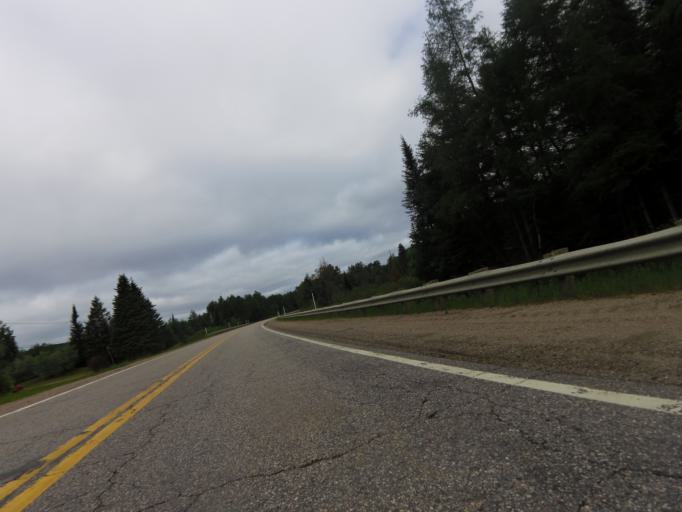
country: CA
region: Quebec
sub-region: Outaouais
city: Shawville
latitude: 45.9072
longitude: -76.3064
